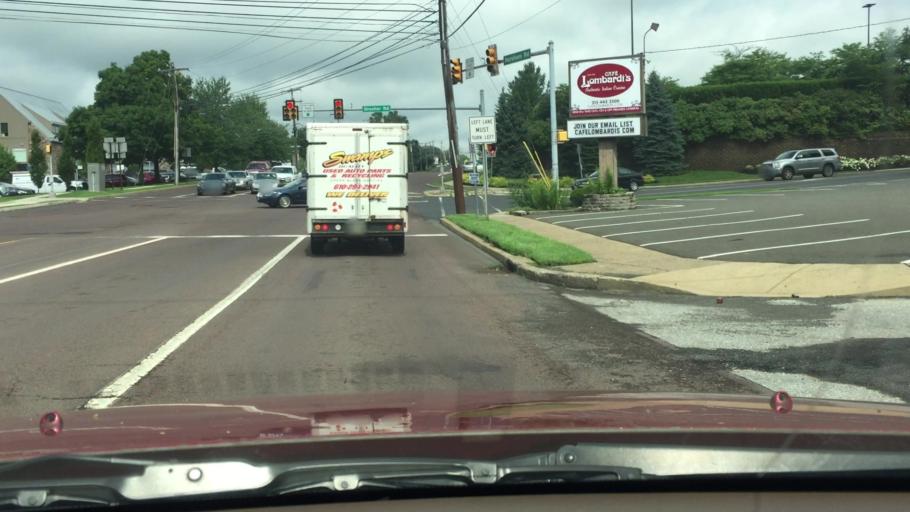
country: US
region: Pennsylvania
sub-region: Montgomery County
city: Horsham
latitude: 40.1805
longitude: -75.1329
